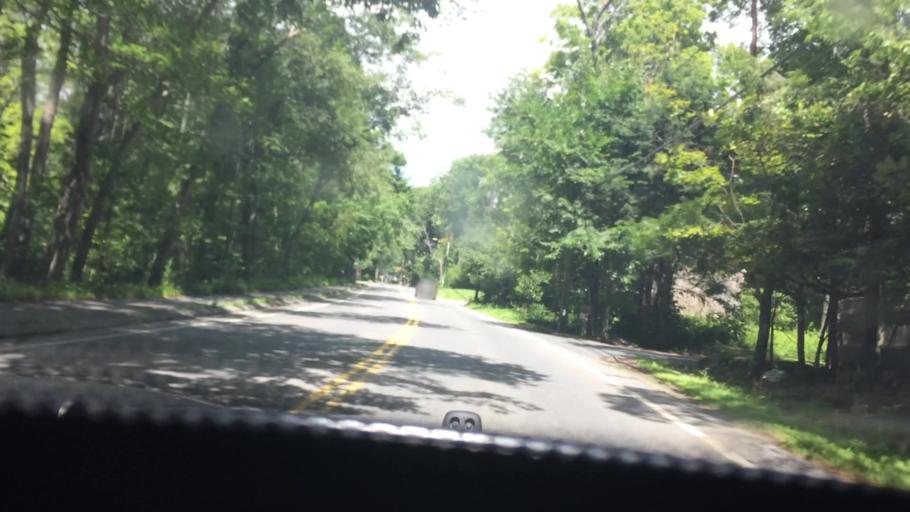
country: US
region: Massachusetts
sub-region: Middlesex County
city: Sudbury
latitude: 42.3905
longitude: -71.4209
